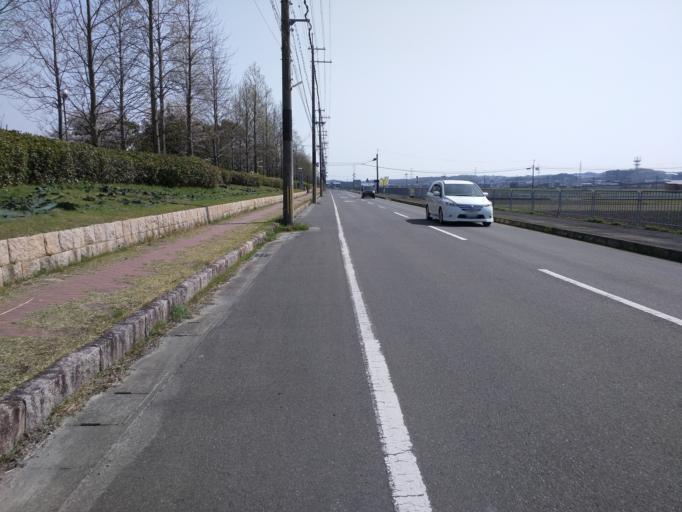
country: JP
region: Kyoto
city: Tanabe
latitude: 34.7755
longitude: 135.7976
